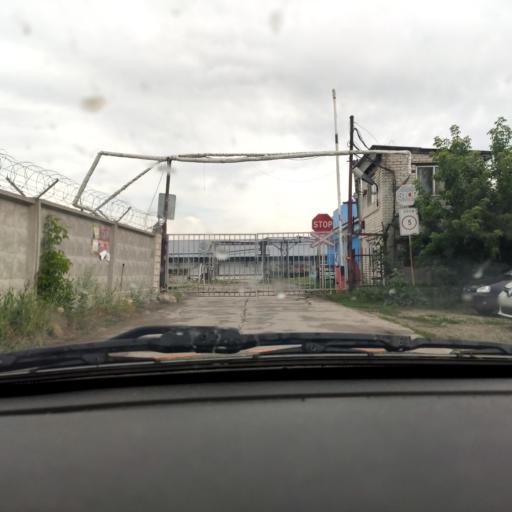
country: RU
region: Samara
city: Tol'yatti
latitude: 53.5332
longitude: 49.4717
